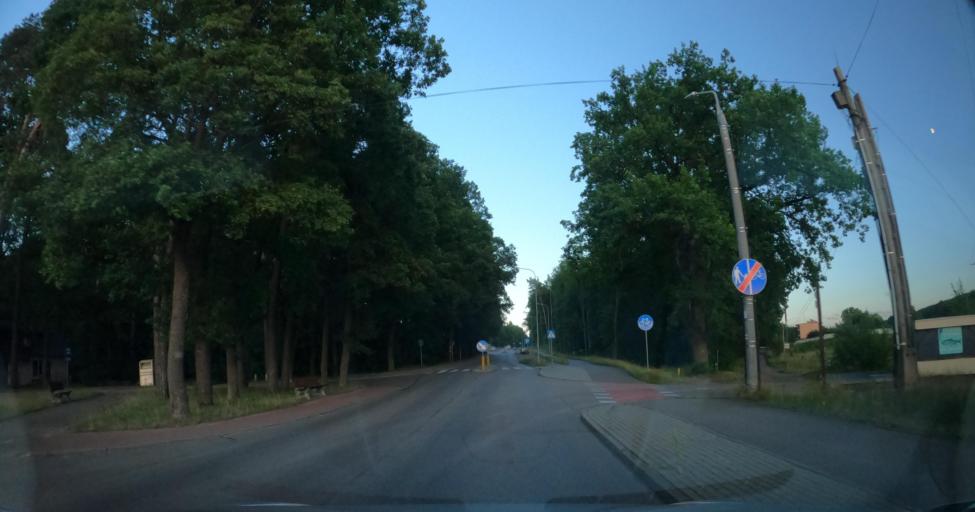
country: PL
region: Pomeranian Voivodeship
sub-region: Powiat leborski
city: Lebork
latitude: 54.5261
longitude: 17.7738
